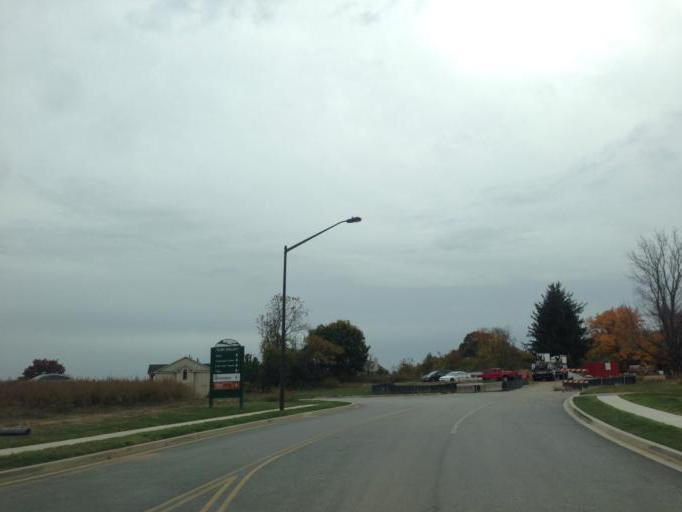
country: US
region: Maryland
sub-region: Howard County
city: Columbia
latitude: 39.3003
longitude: -76.8889
